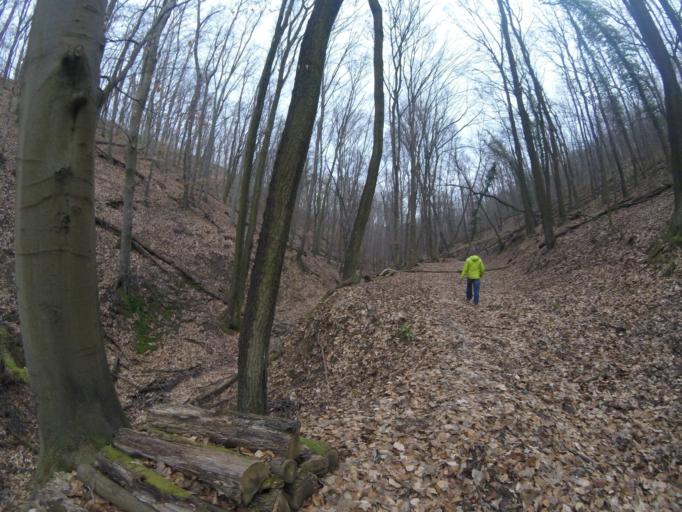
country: HU
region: Baranya
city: Mecseknadasd
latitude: 46.1428
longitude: 18.5169
